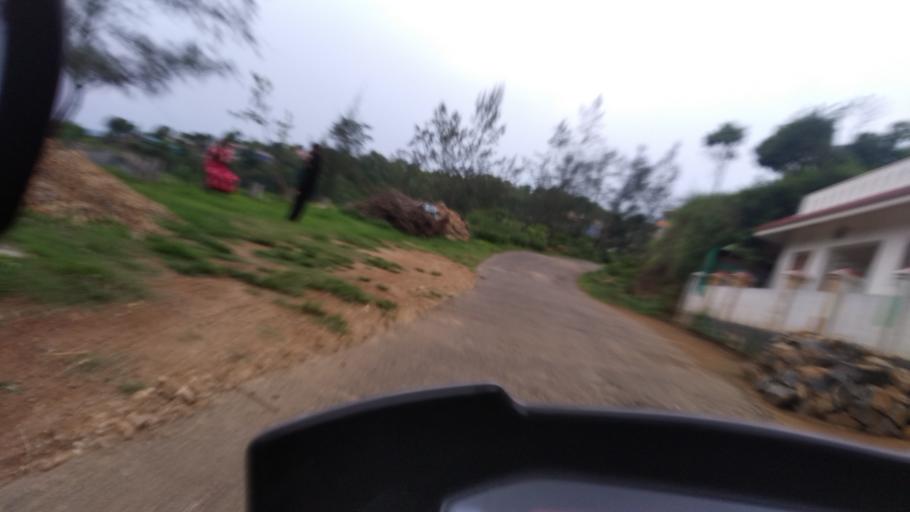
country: IN
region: Tamil Nadu
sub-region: Theni
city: Gudalur
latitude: 9.5461
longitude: 77.0372
